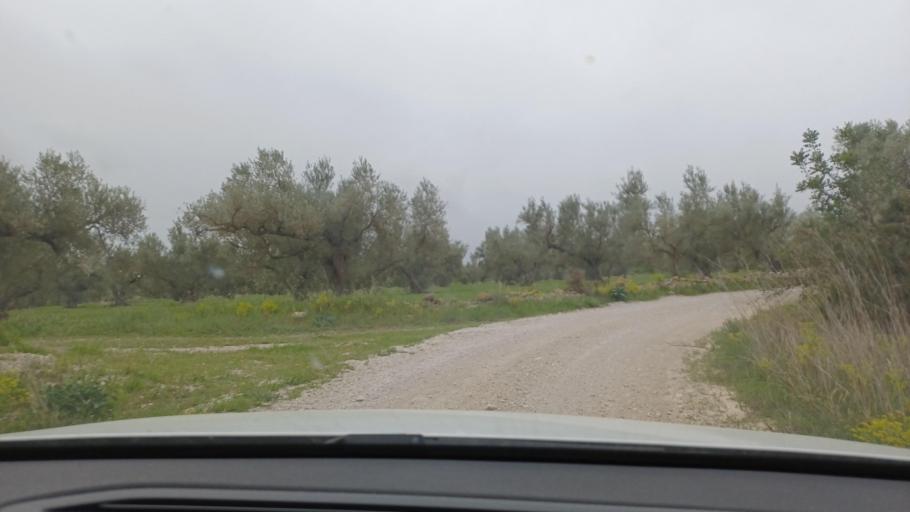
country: ES
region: Catalonia
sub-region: Provincia de Tarragona
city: Mas de Barberans
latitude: 40.8009
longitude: 0.4168
